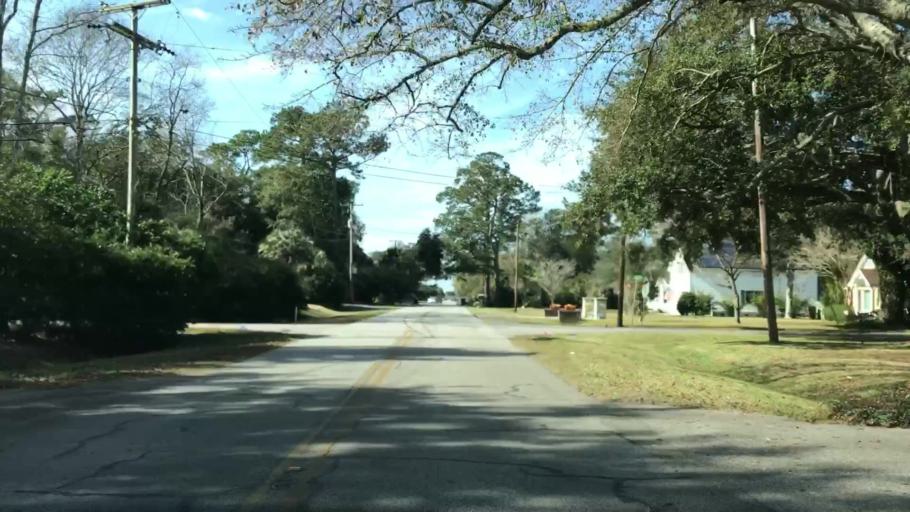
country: US
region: South Carolina
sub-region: Charleston County
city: Charleston
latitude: 32.7719
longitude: -80.0012
